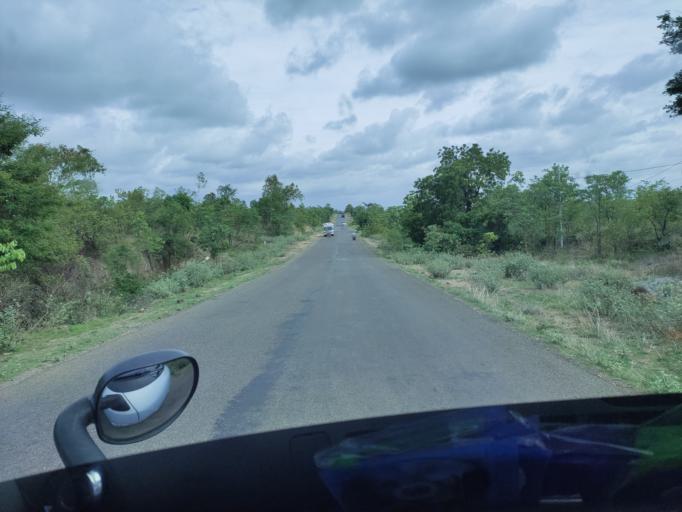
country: MM
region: Magway
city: Chauk
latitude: 20.9716
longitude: 95.0552
